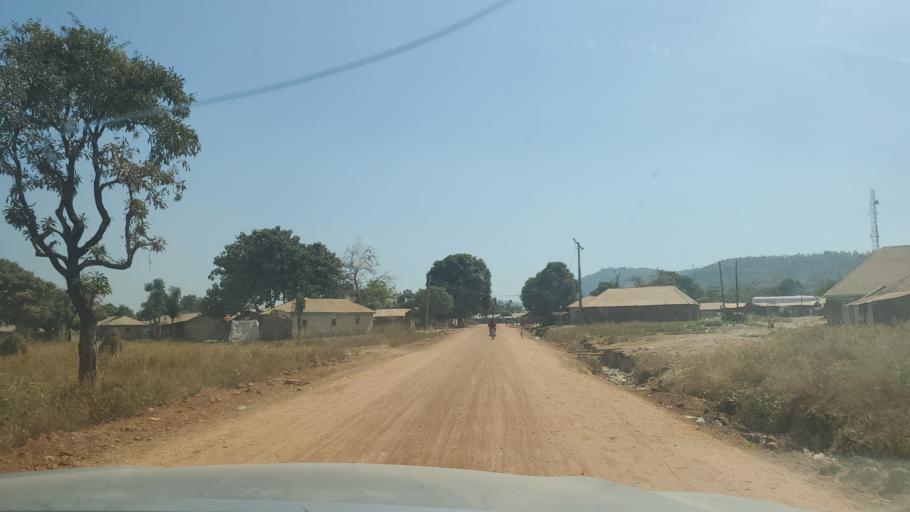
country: NG
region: Niger
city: Gawu Babangida
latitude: 9.2146
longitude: 6.8427
